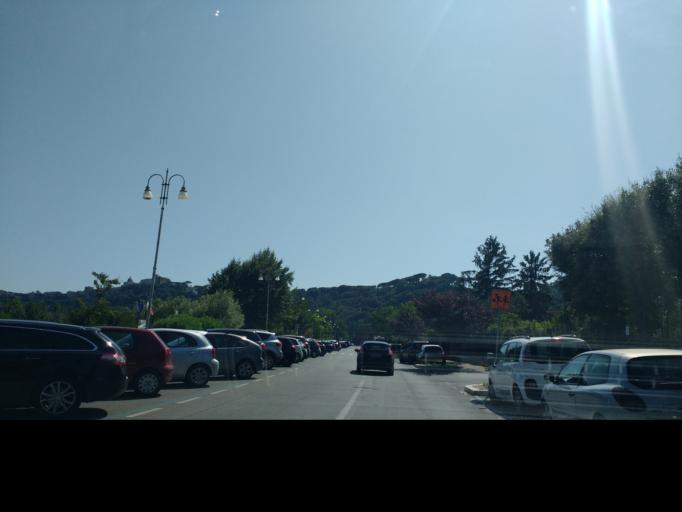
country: IT
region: Latium
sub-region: Citta metropolitana di Roma Capitale
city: Castel Gandolfo
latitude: 41.7607
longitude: 12.6565
